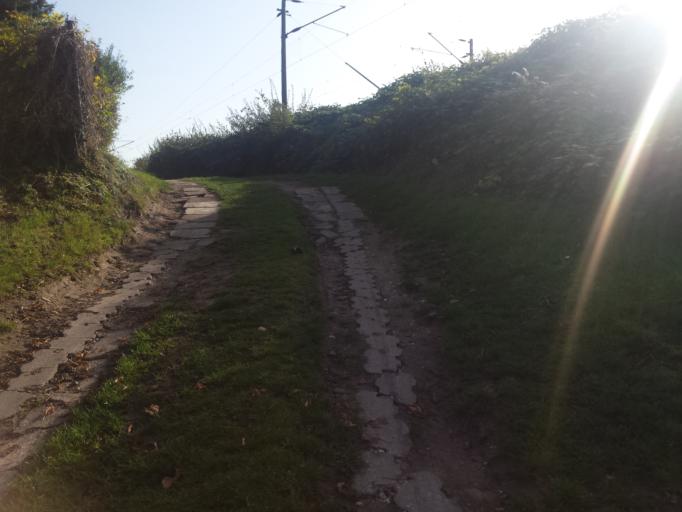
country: DE
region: Saxony
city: Taucha
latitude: 51.3672
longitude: 12.4423
